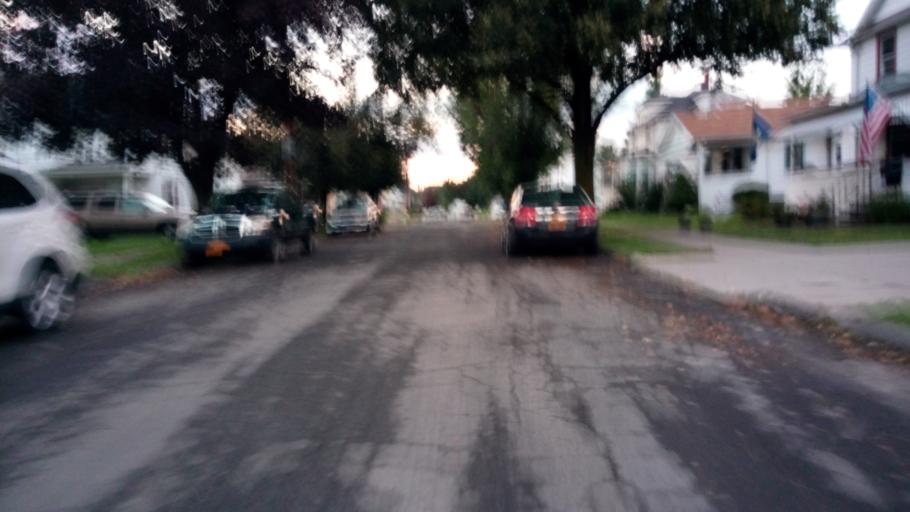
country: US
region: New York
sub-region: Chemung County
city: Elmira
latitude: 42.1012
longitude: -76.8225
